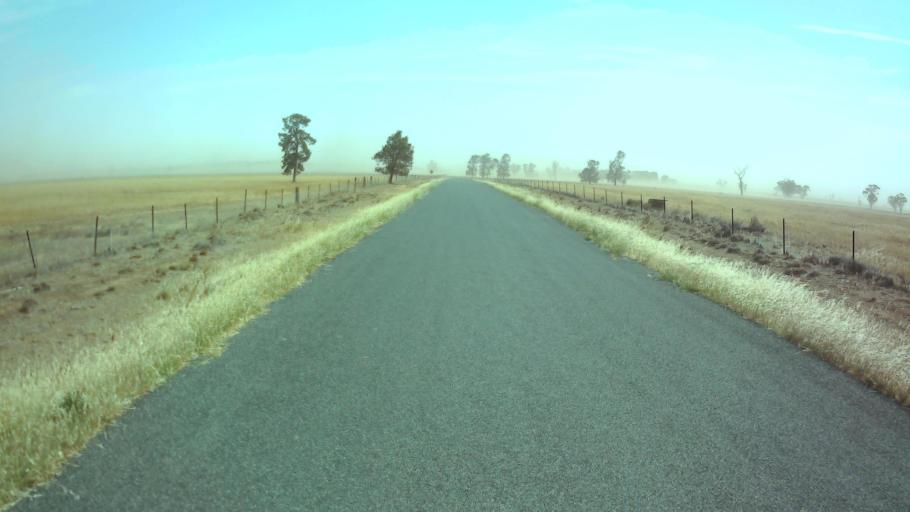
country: AU
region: New South Wales
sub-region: Weddin
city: Grenfell
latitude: -33.7403
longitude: 147.9928
